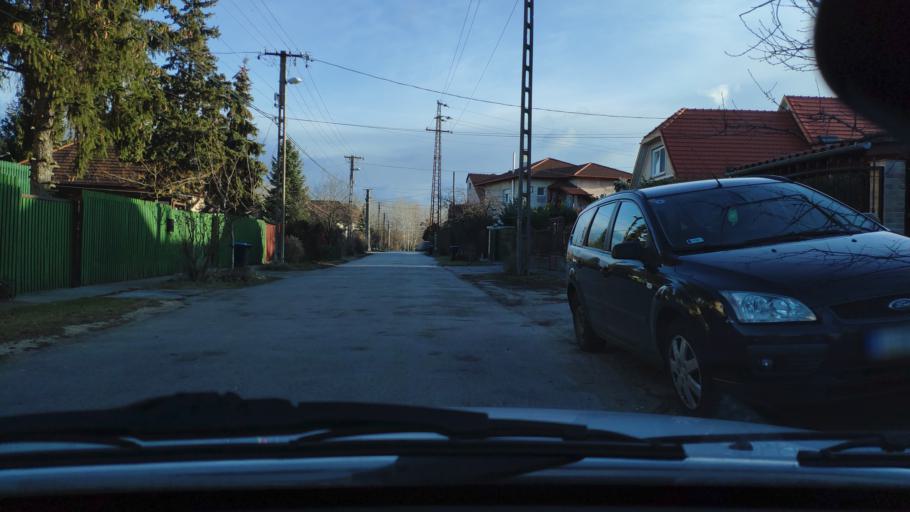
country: HU
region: Budapest
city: Budapest XXIII. keruelet
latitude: 47.3958
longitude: 19.1052
